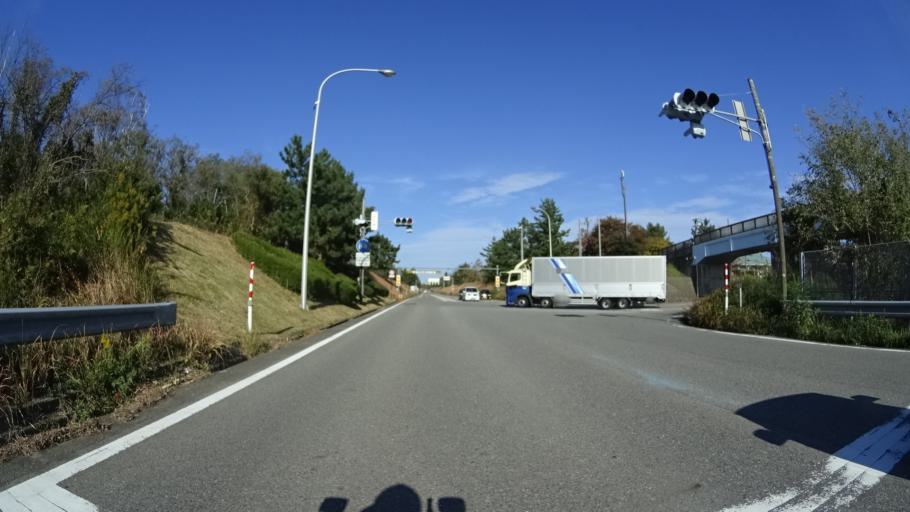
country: JP
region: Ishikawa
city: Kanazawa-shi
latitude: 36.6401
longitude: 136.6319
